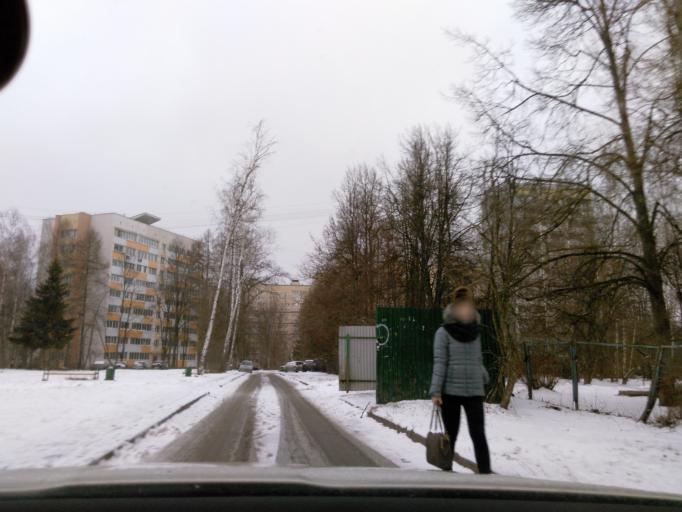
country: RU
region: Moskovskaya
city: Rzhavki
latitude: 55.9972
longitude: 37.2177
